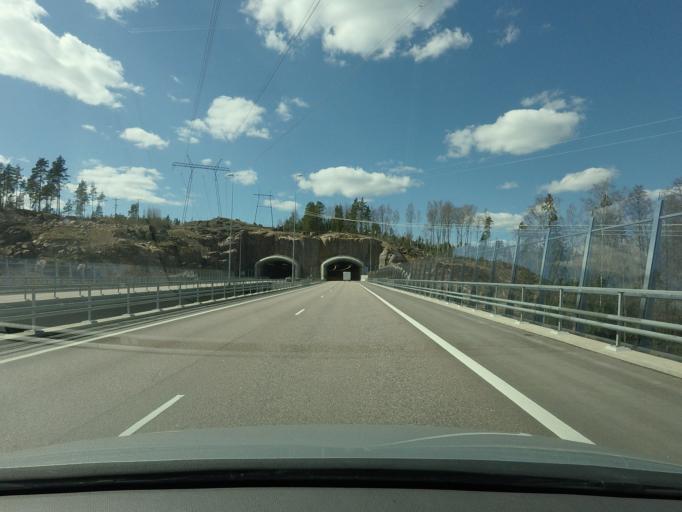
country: FI
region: Uusimaa
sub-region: Loviisa
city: Ruotsinpyhtaeae
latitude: 60.4924
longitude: 26.4472
